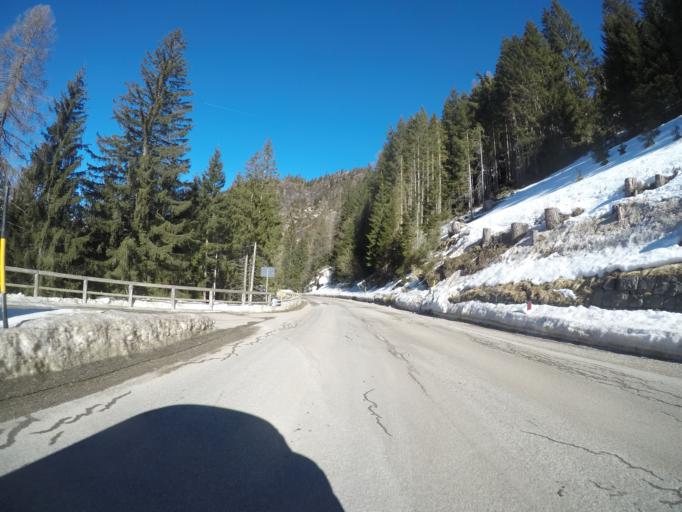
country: IT
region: Veneto
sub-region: Provincia di Belluno
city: Colle Santa Lucia
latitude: 46.4446
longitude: 12.0011
